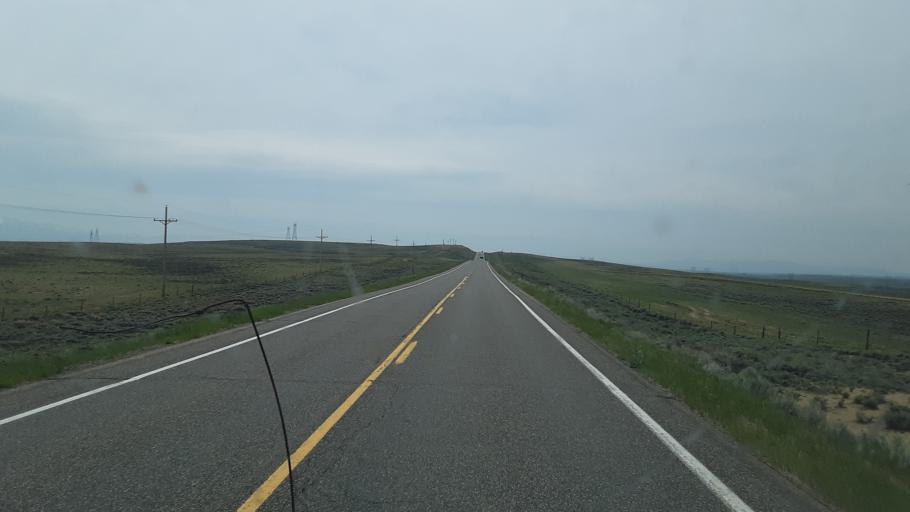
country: US
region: Colorado
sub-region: Jackson County
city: Walden
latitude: 40.8265
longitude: -106.2982
